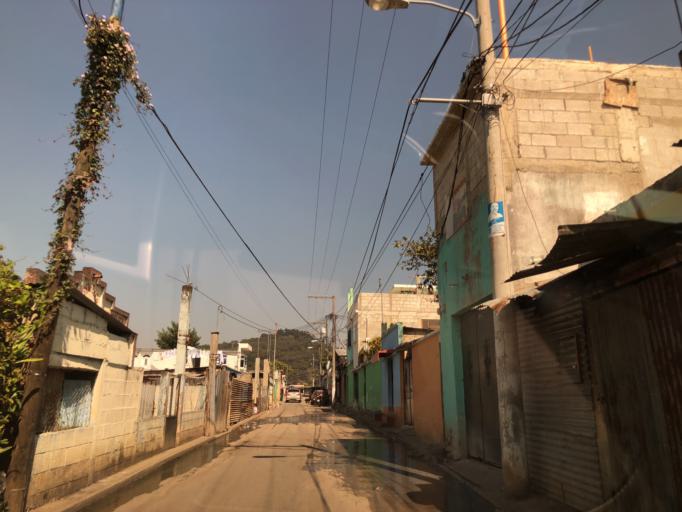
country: GT
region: Guatemala
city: Santa Catarina Pinula
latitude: 14.5397
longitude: -90.5068
